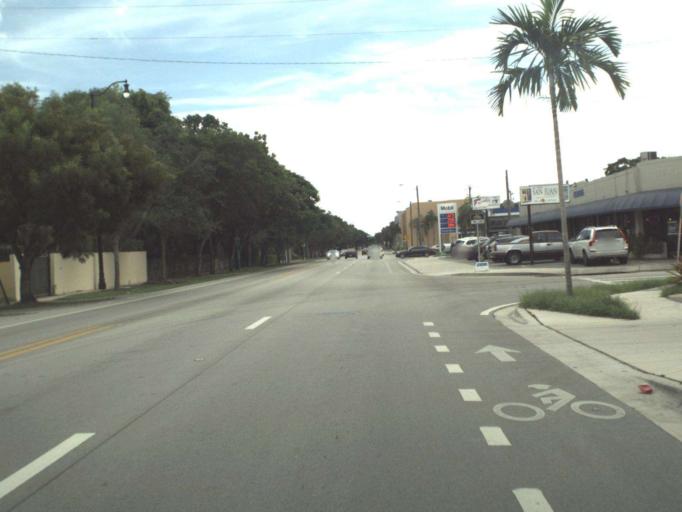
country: US
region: Florida
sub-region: Miami-Dade County
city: West Miami
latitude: 25.7603
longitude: -80.2878
